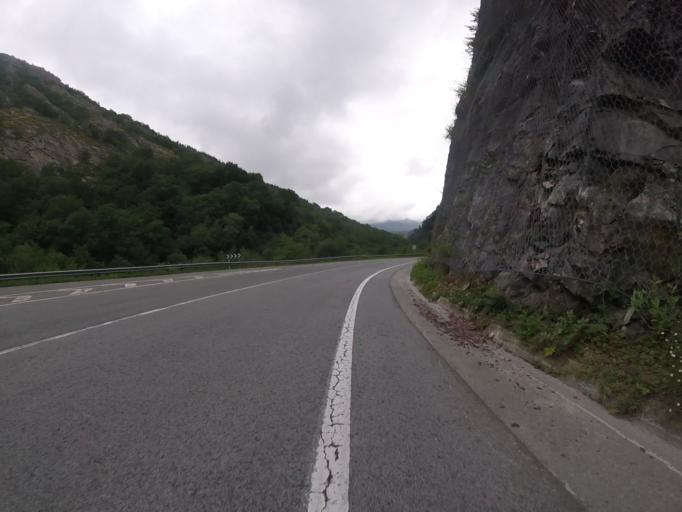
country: ES
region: Navarre
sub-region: Provincia de Navarra
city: Saldias
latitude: 43.1093
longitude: -1.7655
